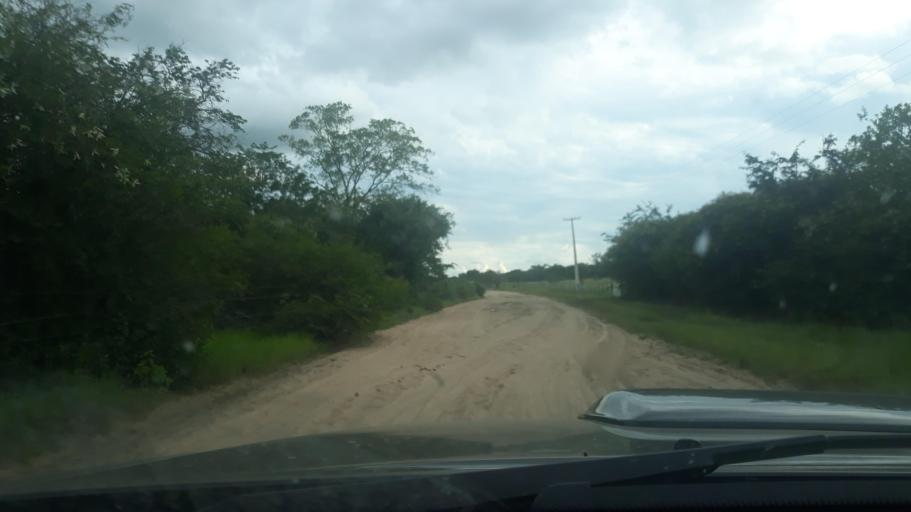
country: BR
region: Bahia
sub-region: Riacho De Santana
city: Riacho de Santana
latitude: -13.8764
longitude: -43.0206
